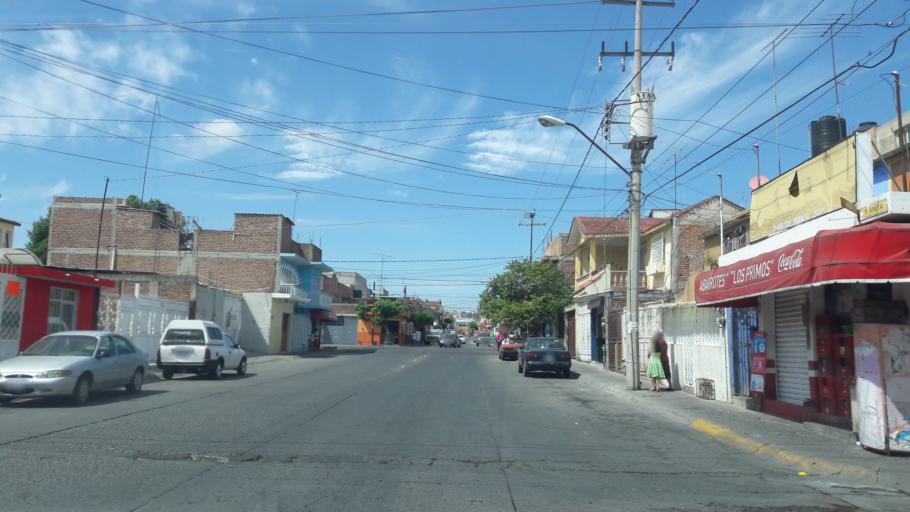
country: MX
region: Guanajuato
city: Leon
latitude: 21.1086
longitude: -101.7015
